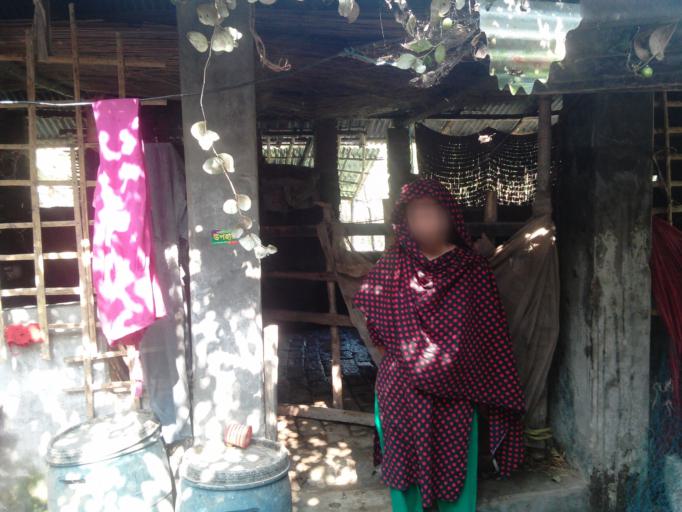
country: BD
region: Khulna
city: Kesabpur
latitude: 22.7700
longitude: 89.2313
